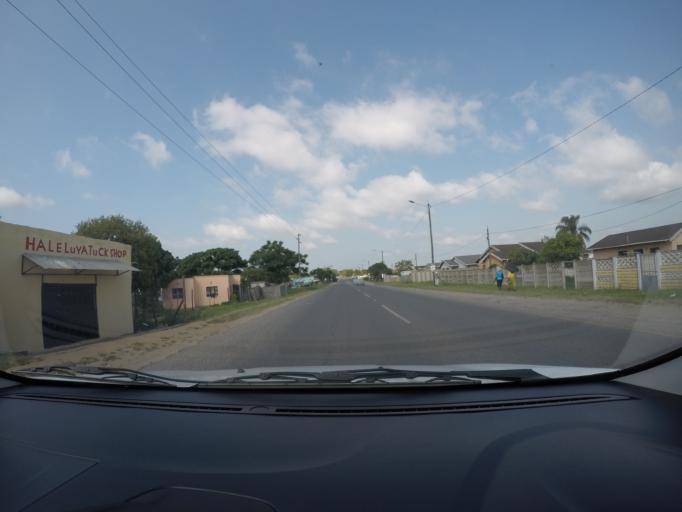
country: ZA
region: KwaZulu-Natal
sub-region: uThungulu District Municipality
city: eSikhawini
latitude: -28.8716
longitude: 31.9225
